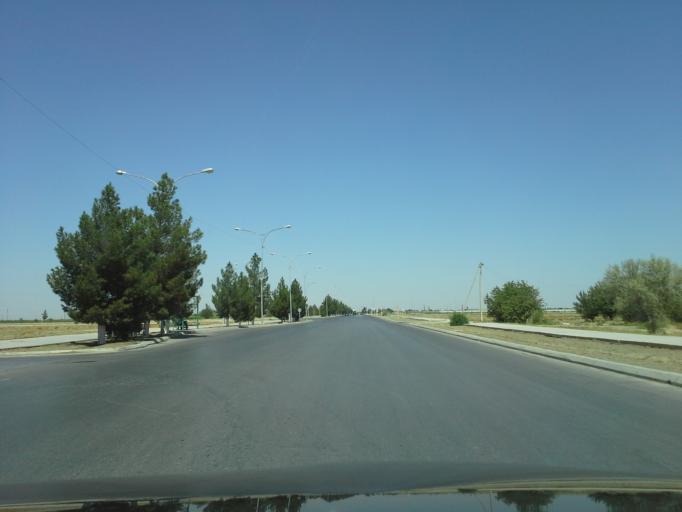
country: TM
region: Ahal
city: Ashgabat
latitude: 37.9958
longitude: 58.3246
